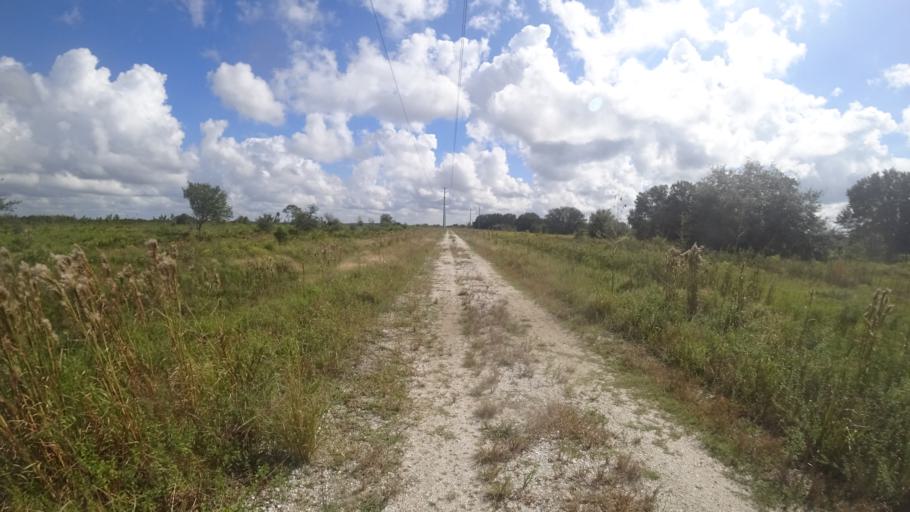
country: US
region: Florida
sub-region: Hillsborough County
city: Wimauma
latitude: 27.5157
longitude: -82.1074
